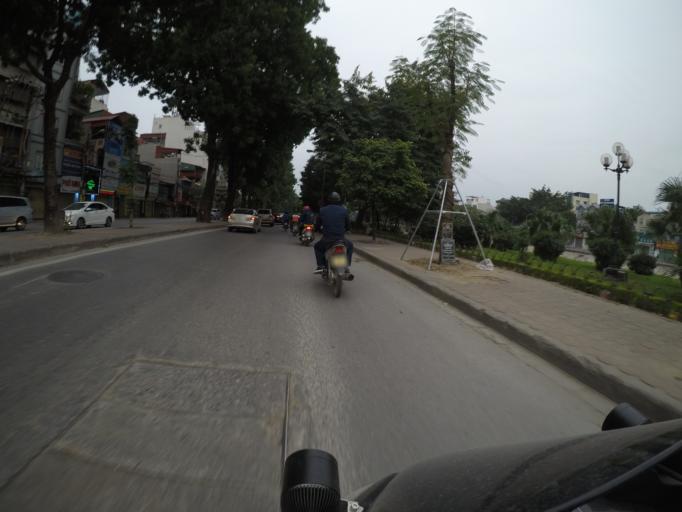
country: VN
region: Ha Noi
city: Cau Giay
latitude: 21.0240
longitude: 105.7984
